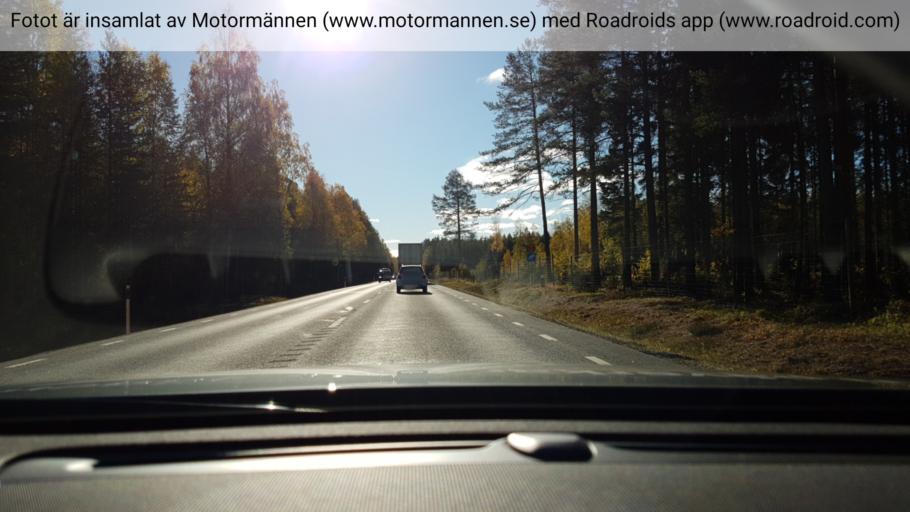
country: SE
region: Vaesterbotten
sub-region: Skelleftea Kommun
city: Burea
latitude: 64.5495
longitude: 21.2471
